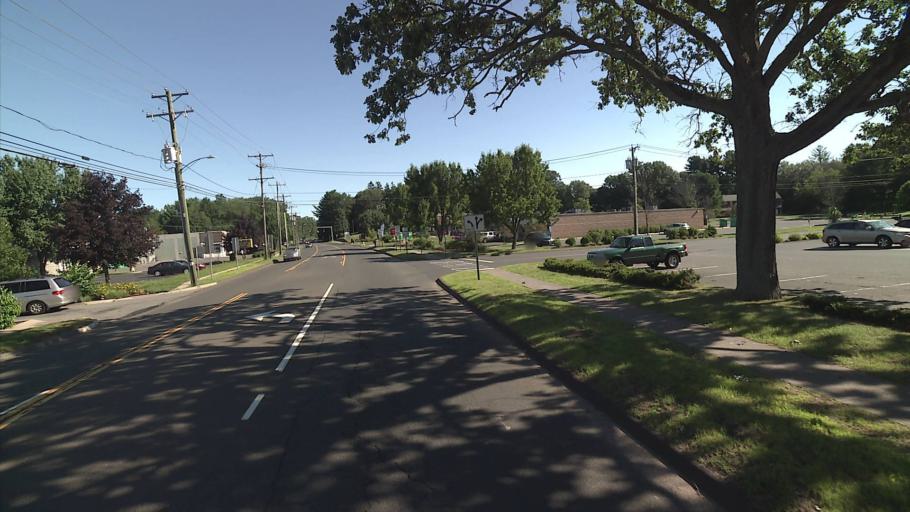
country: US
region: Connecticut
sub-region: New Haven County
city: Cheshire
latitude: 41.4804
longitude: -72.9057
